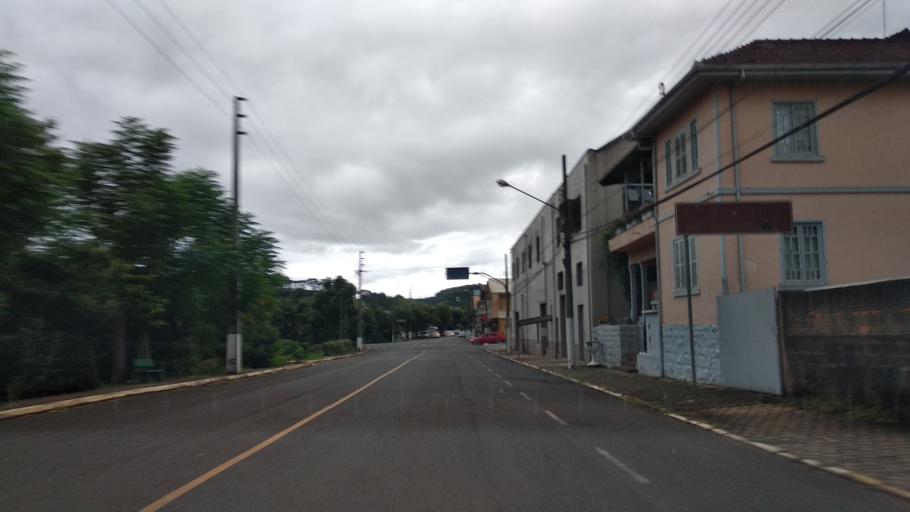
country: BR
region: Santa Catarina
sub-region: Videira
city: Videira
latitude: -27.0472
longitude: -51.2300
